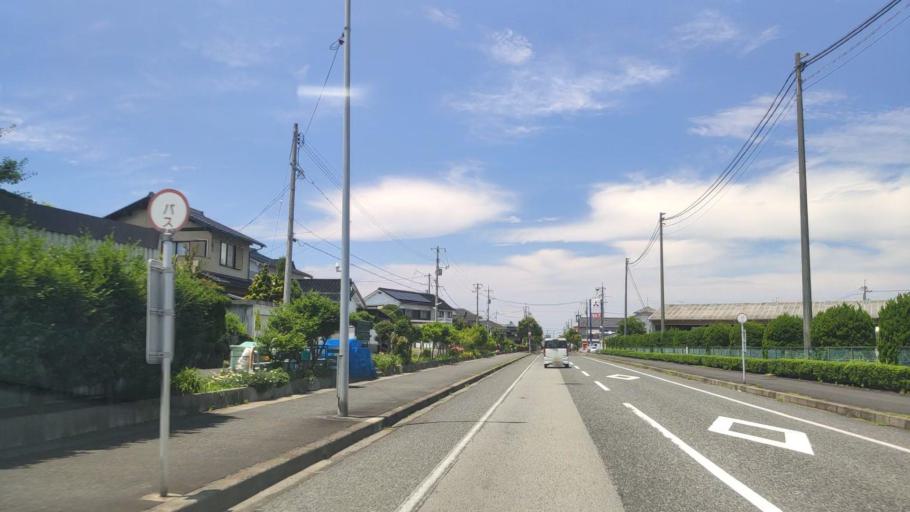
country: JP
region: Tottori
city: Tottori
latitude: 35.4754
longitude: 134.2373
